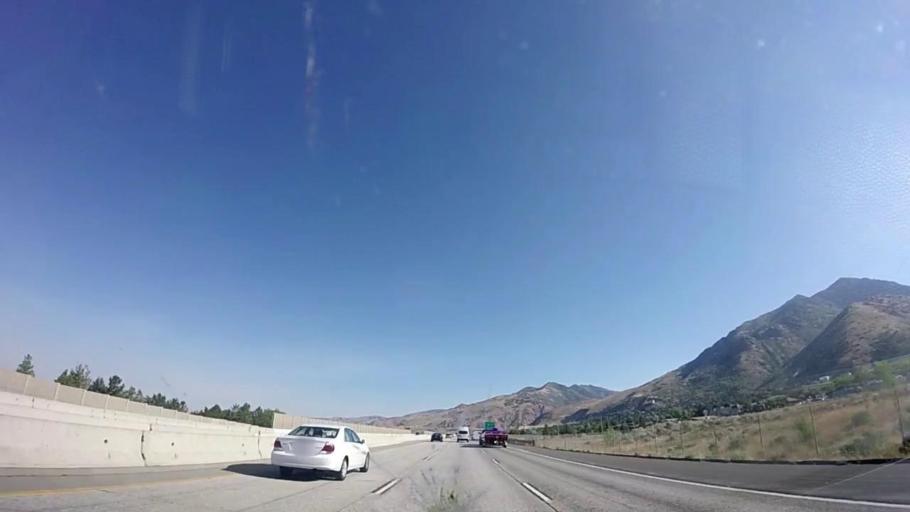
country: US
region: Utah
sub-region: Salt Lake County
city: Mount Olympus
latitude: 40.6841
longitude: -111.7975
